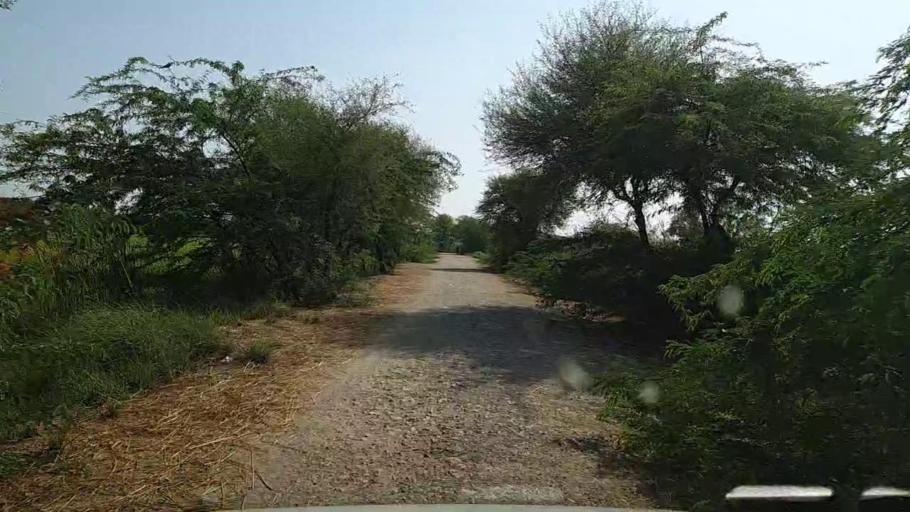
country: PK
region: Sindh
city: Kario
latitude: 24.8176
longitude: 68.5442
